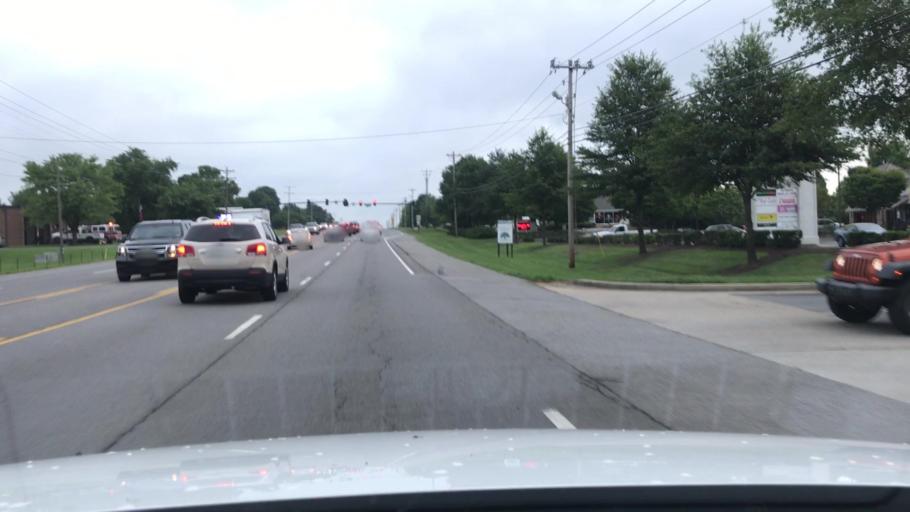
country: US
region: Tennessee
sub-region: Sumner County
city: Gallatin
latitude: 36.3590
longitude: -86.4998
